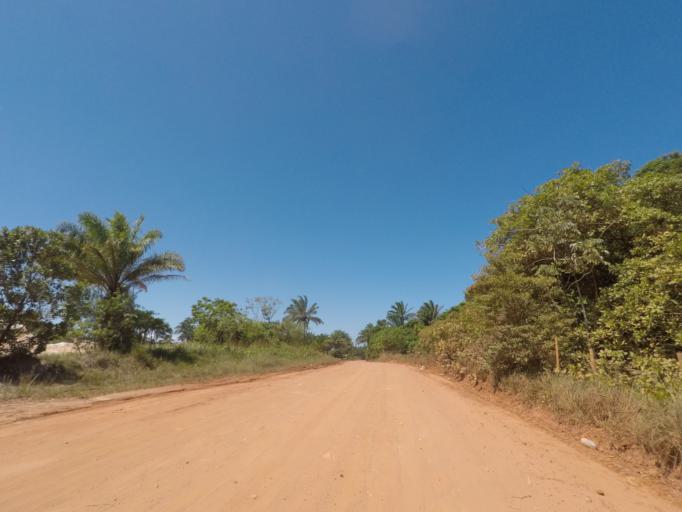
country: BR
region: Bahia
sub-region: Camamu
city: Camamu
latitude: -13.9580
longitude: -38.9461
